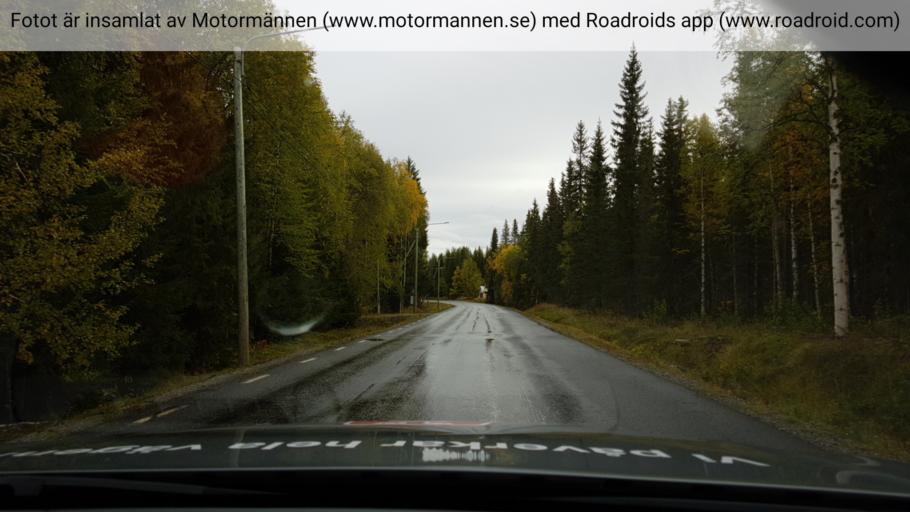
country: SE
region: Vaesterbotten
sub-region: Vilhelmina Kommun
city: Sjoberg
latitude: 64.6534
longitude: 16.3231
